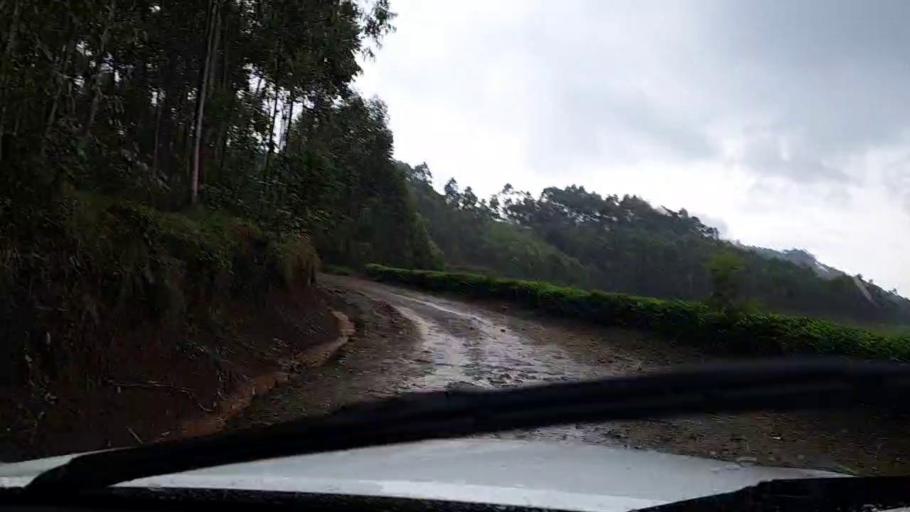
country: RW
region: Western Province
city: Cyangugu
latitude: -2.4727
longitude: 29.0334
